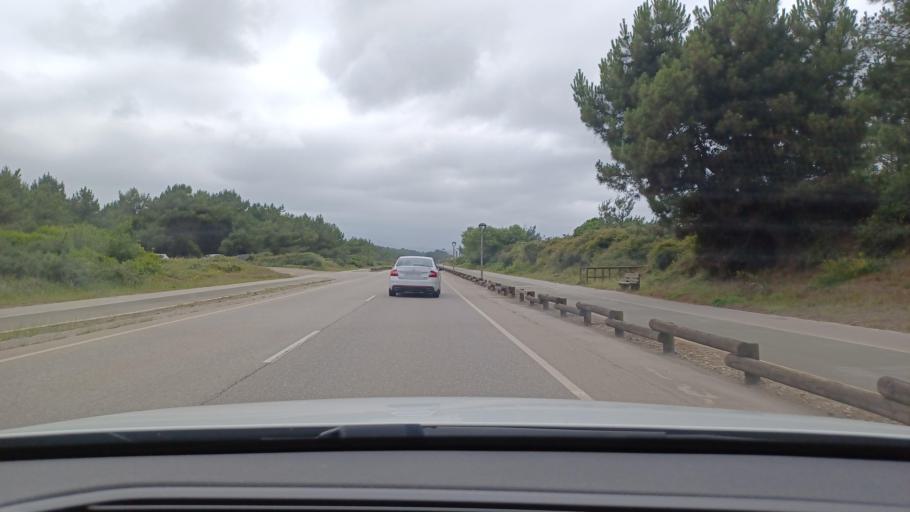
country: ES
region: Asturias
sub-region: Province of Asturias
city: Aviles
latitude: 43.5860
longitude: -5.9396
